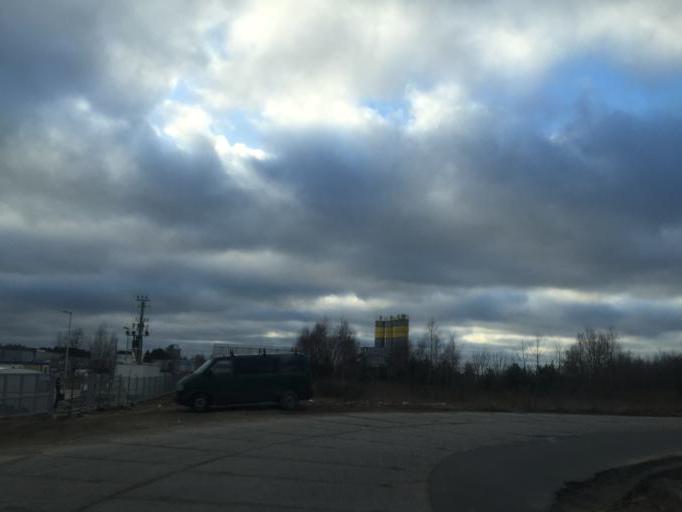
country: PL
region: Pomeranian Voivodeship
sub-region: Gdynia
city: Wielki Kack
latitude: 54.4140
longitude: 18.4709
